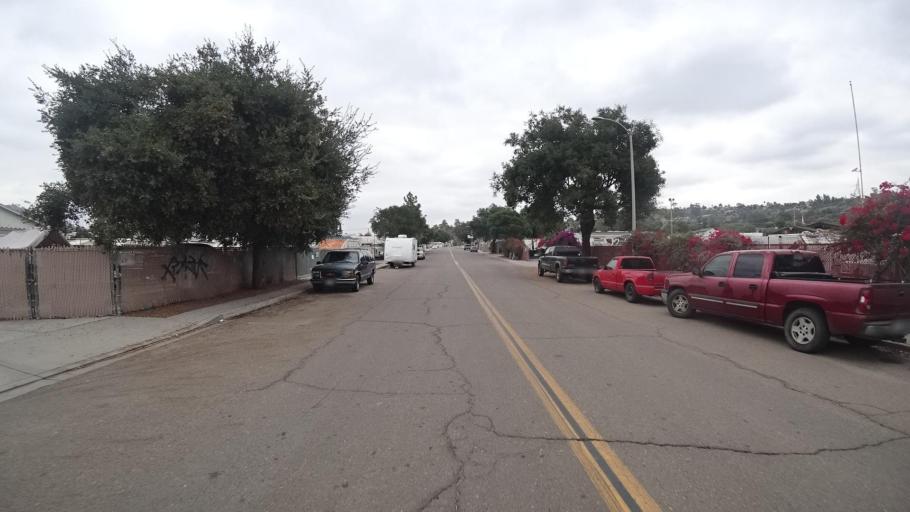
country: US
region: California
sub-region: San Diego County
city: Spring Valley
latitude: 32.7420
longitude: -117.0010
